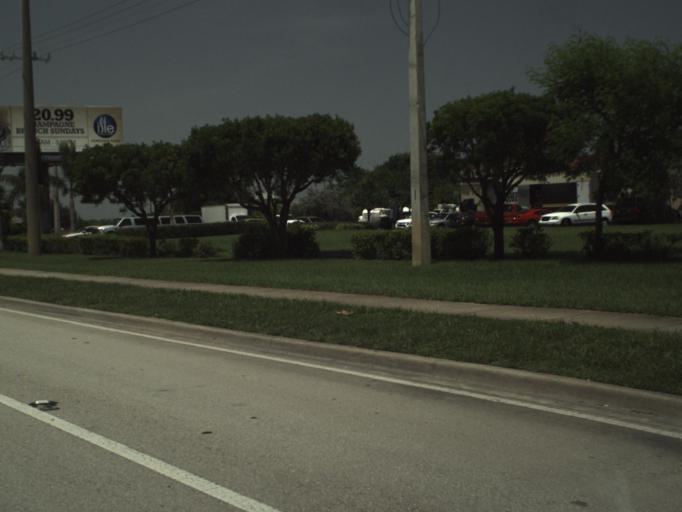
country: US
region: Florida
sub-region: Broward County
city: Tedder
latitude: 26.2882
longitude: -80.1523
